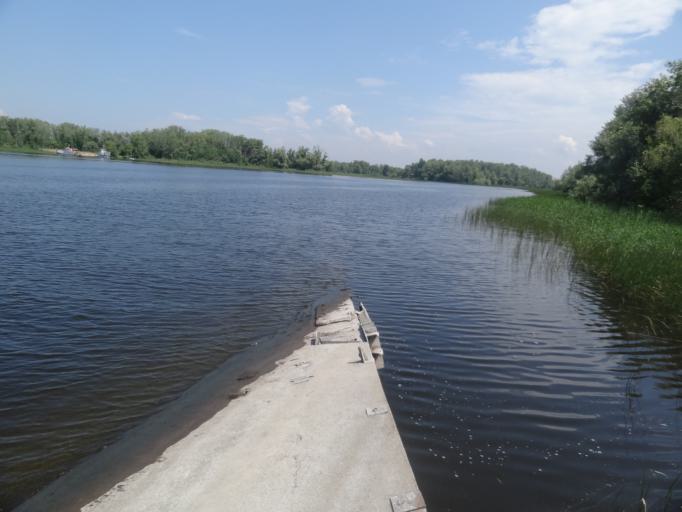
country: RU
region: Saratov
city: Engel's
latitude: 51.5486
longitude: 46.1179
